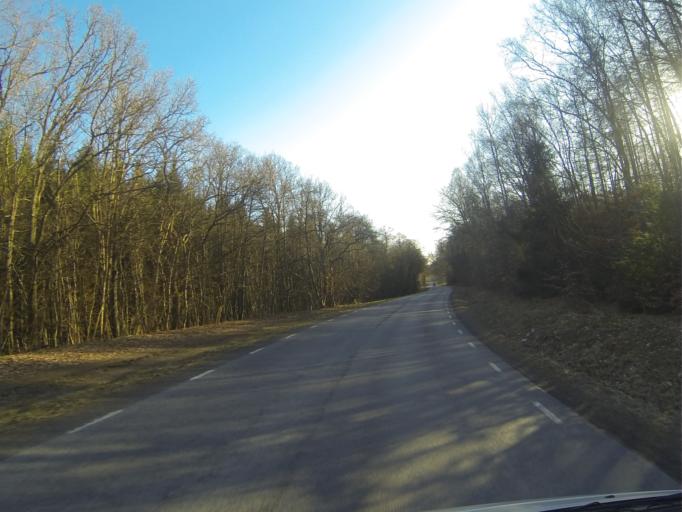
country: SE
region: Skane
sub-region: Horby Kommun
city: Hoerby
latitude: 55.8714
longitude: 13.6650
